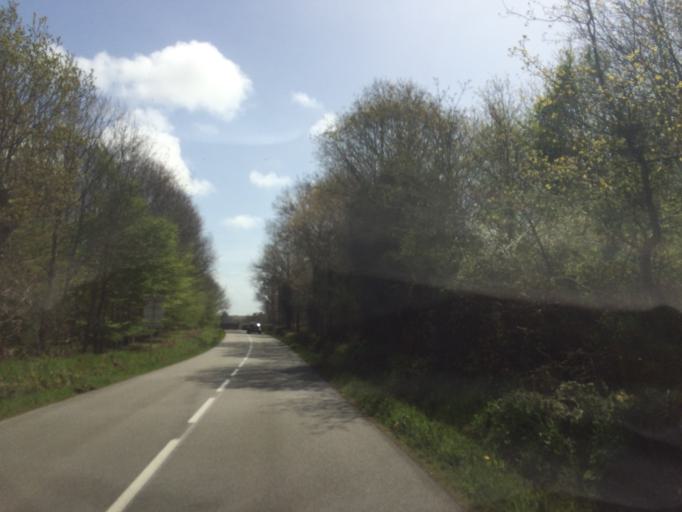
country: FR
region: Brittany
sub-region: Departement du Morbihan
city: Ploemel
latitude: 47.6349
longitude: -3.0477
